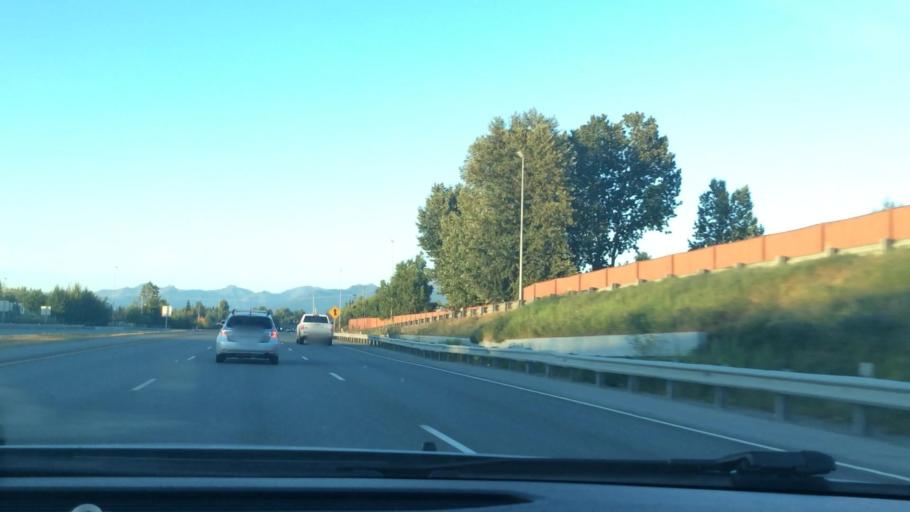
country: US
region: Alaska
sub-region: Anchorage Municipality
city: Anchorage
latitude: 61.2212
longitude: -149.8074
